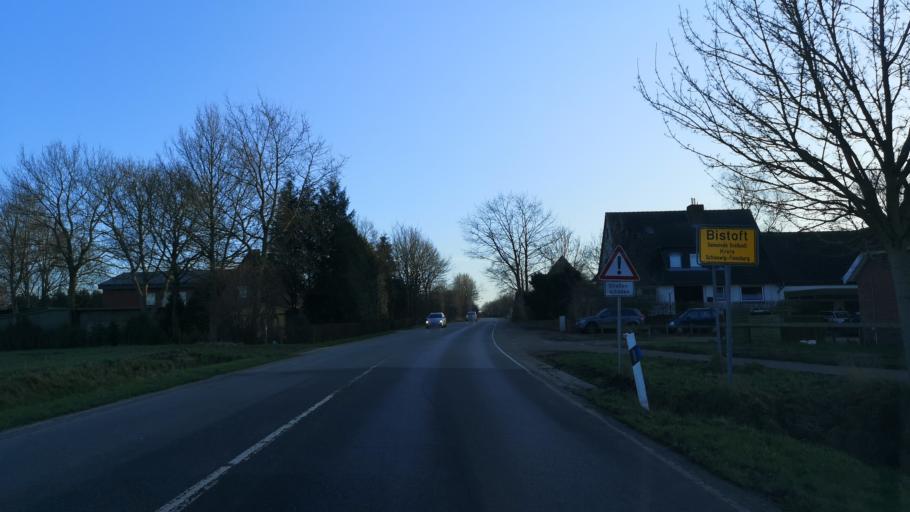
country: DE
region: Schleswig-Holstein
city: Grosssolt
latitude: 54.7059
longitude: 9.5314
